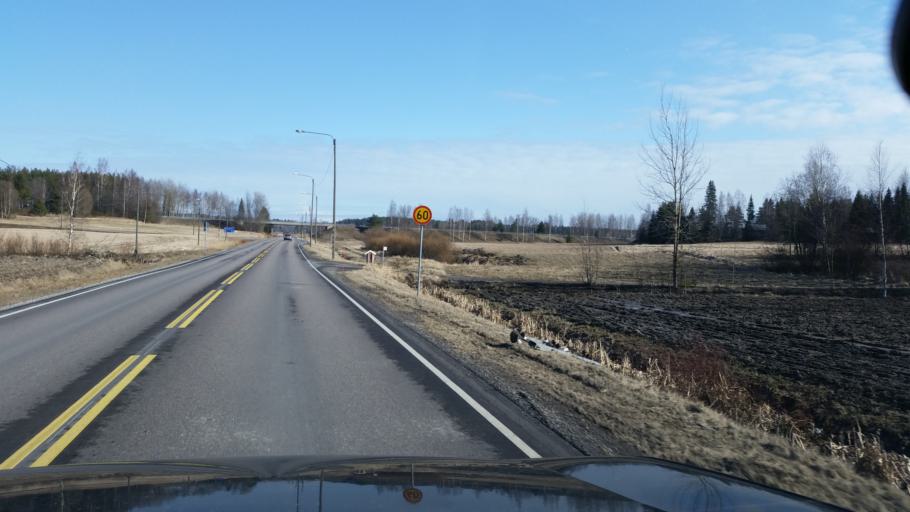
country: FI
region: Uusimaa
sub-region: Raaseporin
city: Inga
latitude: 60.0466
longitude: 23.9464
